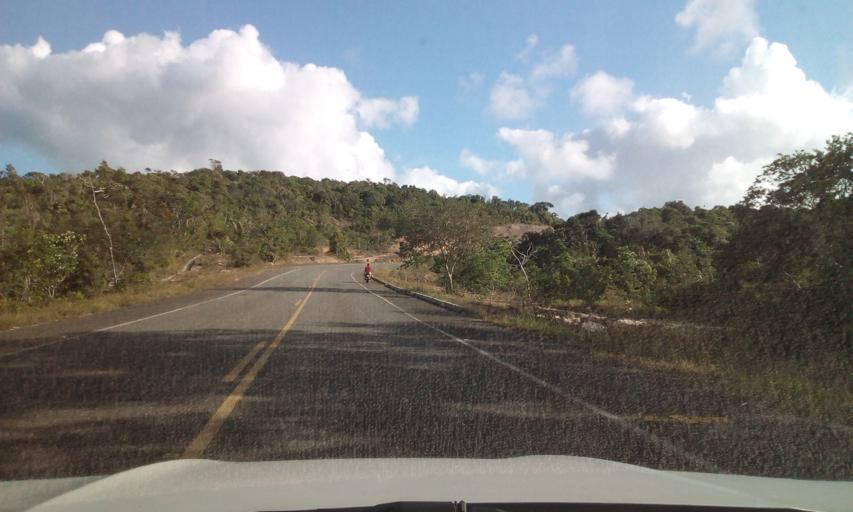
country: BR
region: Bahia
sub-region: Conde
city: Conde
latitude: -12.0865
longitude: -37.7727
